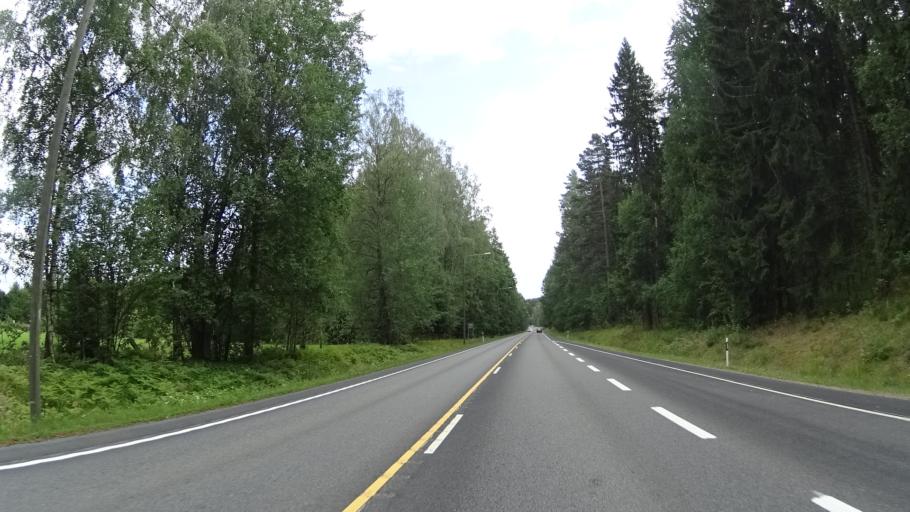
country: FI
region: Pirkanmaa
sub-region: Tampere
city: Kangasala
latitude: 61.4256
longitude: 24.1356
